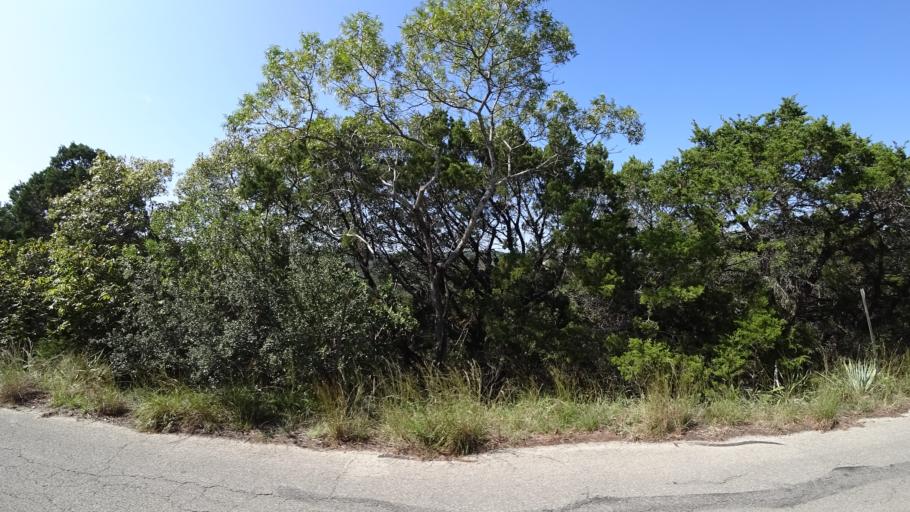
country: US
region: Texas
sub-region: Travis County
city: West Lake Hills
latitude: 30.3042
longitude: -97.8064
